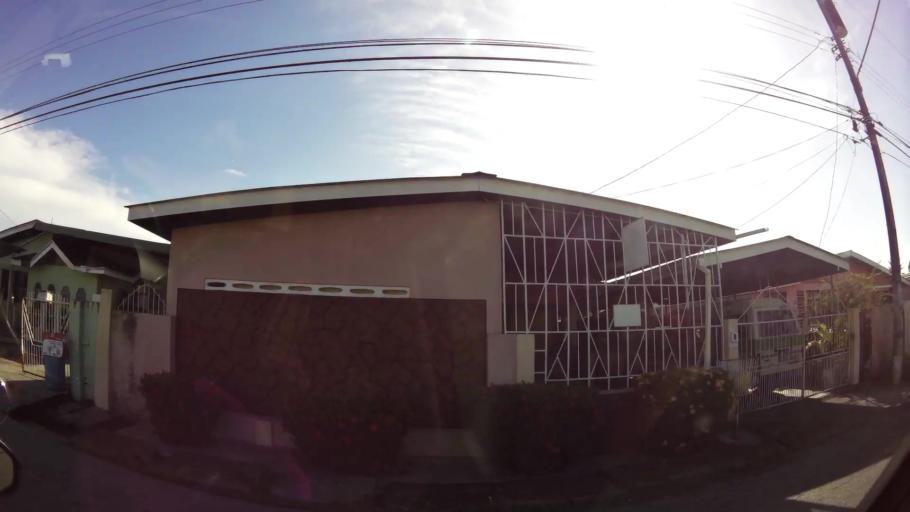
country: TT
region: Chaguanas
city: Chaguanas
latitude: 10.5298
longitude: -61.3911
